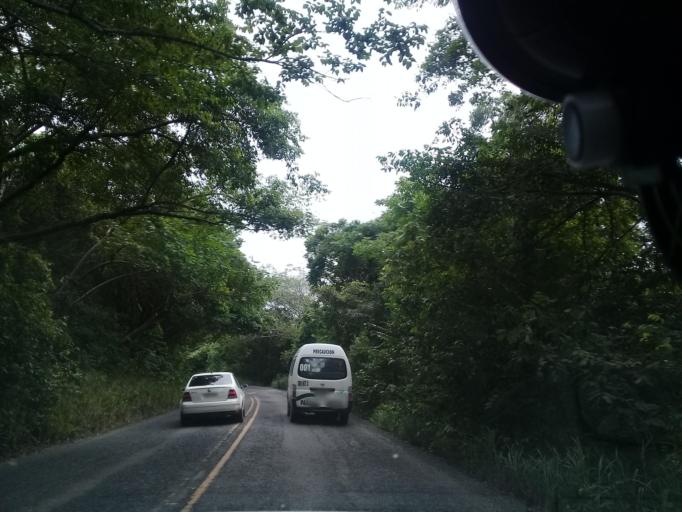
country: MX
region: Veracruz
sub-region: Chalma
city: San Pedro Coyutla
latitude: 21.2020
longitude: -98.3894
